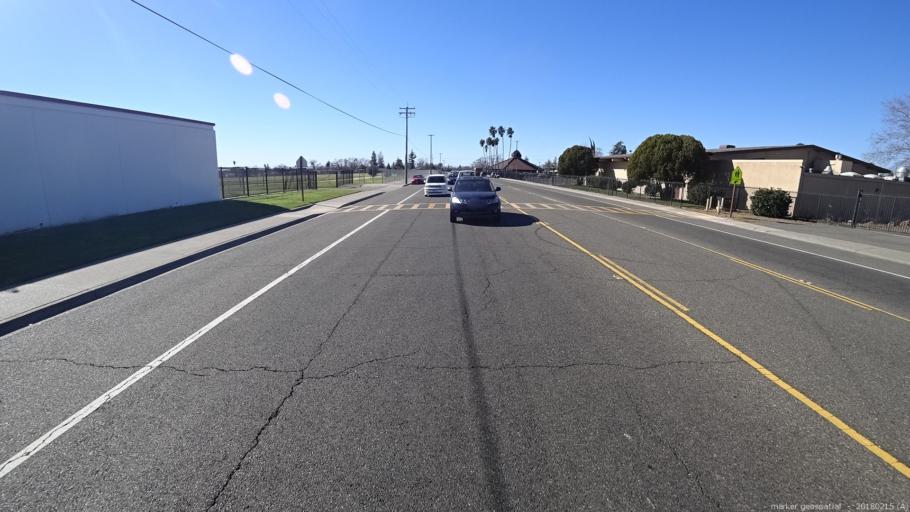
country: US
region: California
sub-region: Sacramento County
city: North Highlands
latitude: 38.6890
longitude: -121.3601
